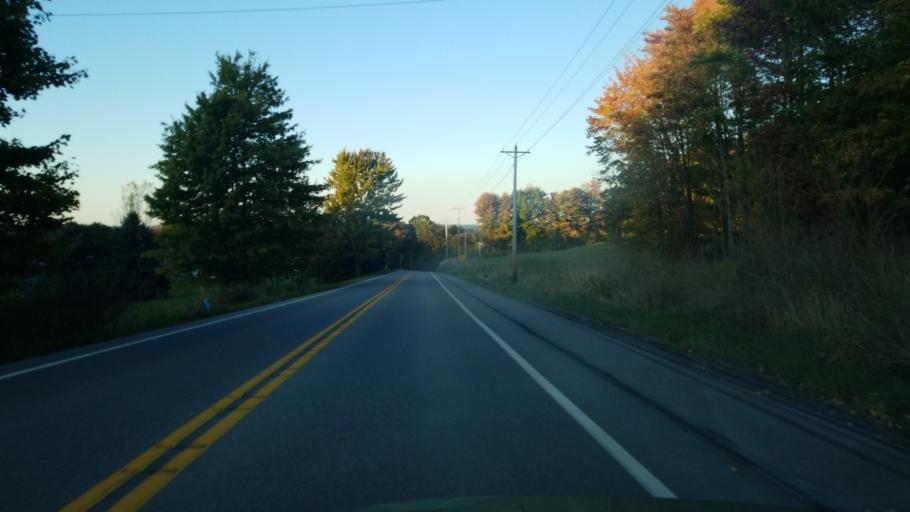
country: US
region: Pennsylvania
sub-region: Jefferson County
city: Reynoldsville
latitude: 41.0593
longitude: -78.9304
